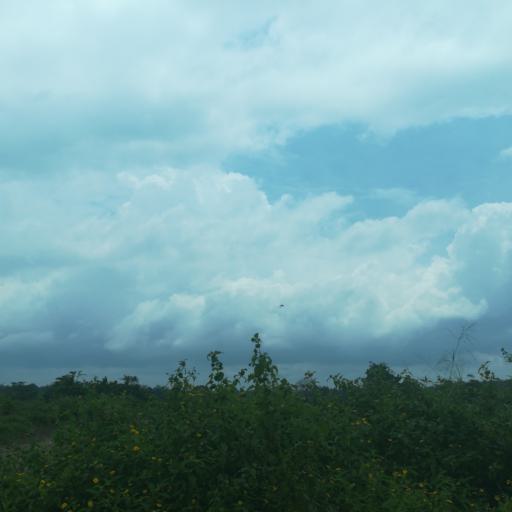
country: NG
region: Lagos
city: Ejirin
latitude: 6.6711
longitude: 3.7999
